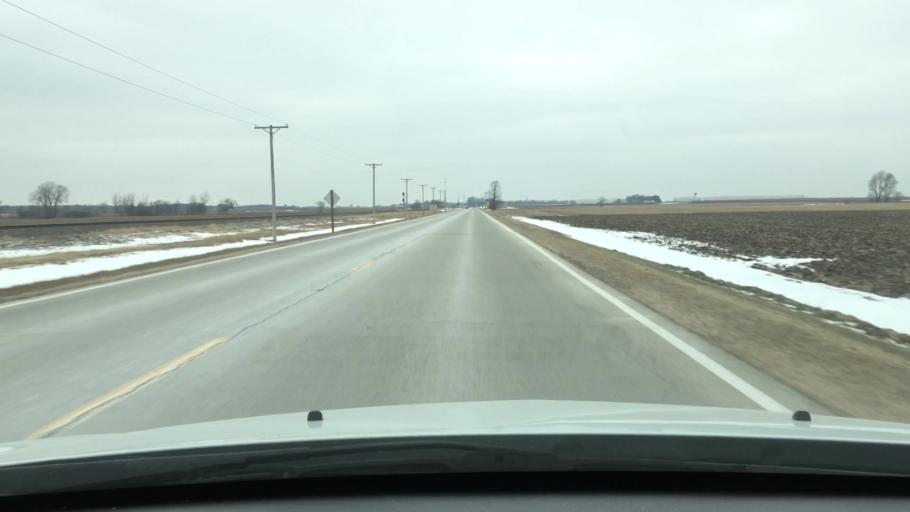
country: US
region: Illinois
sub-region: DeKalb County
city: Waterman
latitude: 41.7689
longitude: -88.8236
